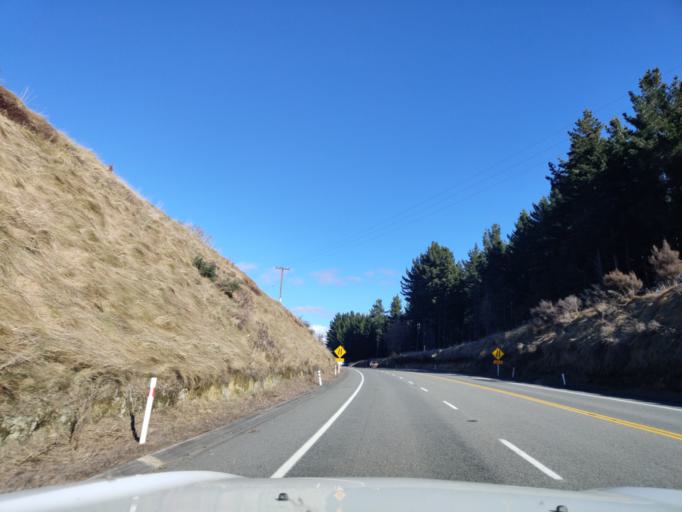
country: NZ
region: Manawatu-Wanganui
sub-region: Ruapehu District
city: Waiouru
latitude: -39.4487
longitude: 175.6789
